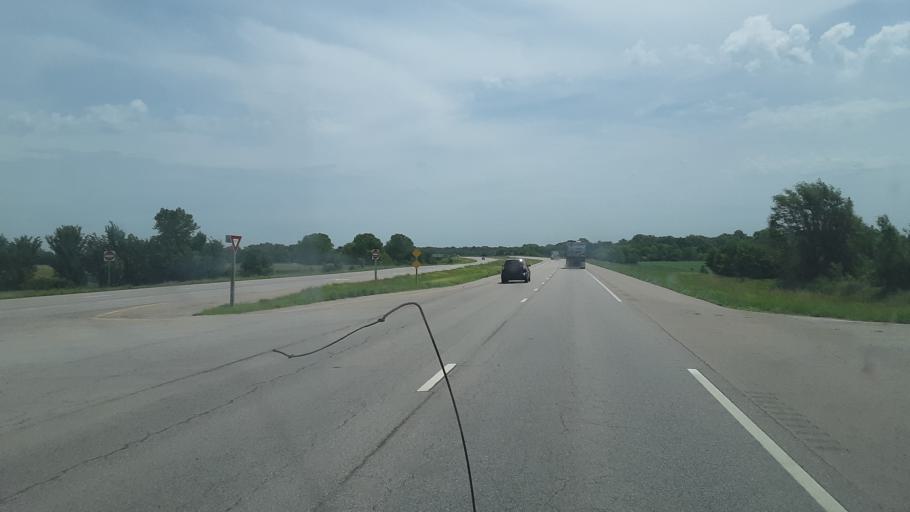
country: US
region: Kansas
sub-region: Butler County
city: Towanda
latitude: 37.7957
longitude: -97.0216
